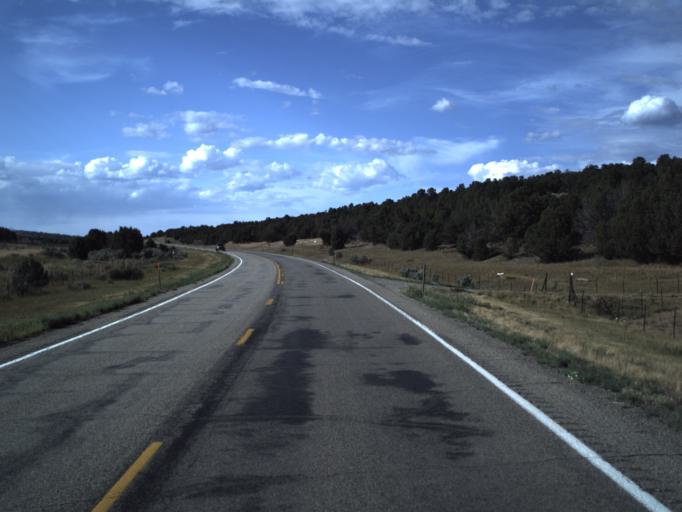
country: US
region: Utah
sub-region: Sanpete County
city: Fairview
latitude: 39.6568
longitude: -111.4503
